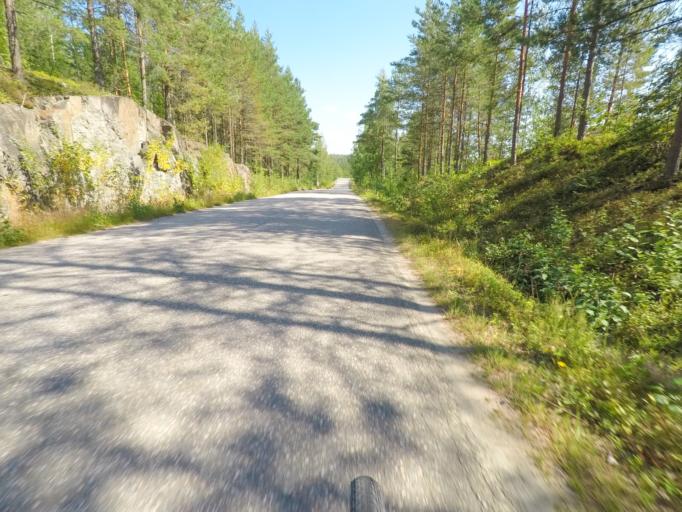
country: FI
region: Southern Savonia
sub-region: Mikkeli
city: Puumala
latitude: 61.4213
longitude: 28.1080
